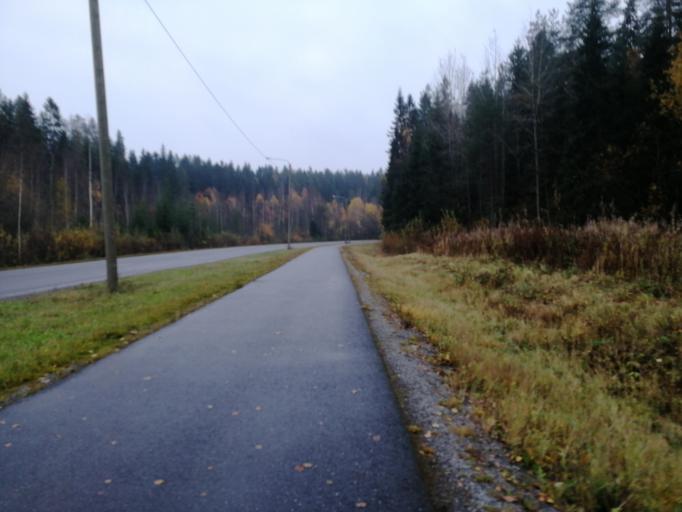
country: FI
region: Pirkanmaa
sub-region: Tampere
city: Tampere
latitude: 61.4473
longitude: 23.8737
